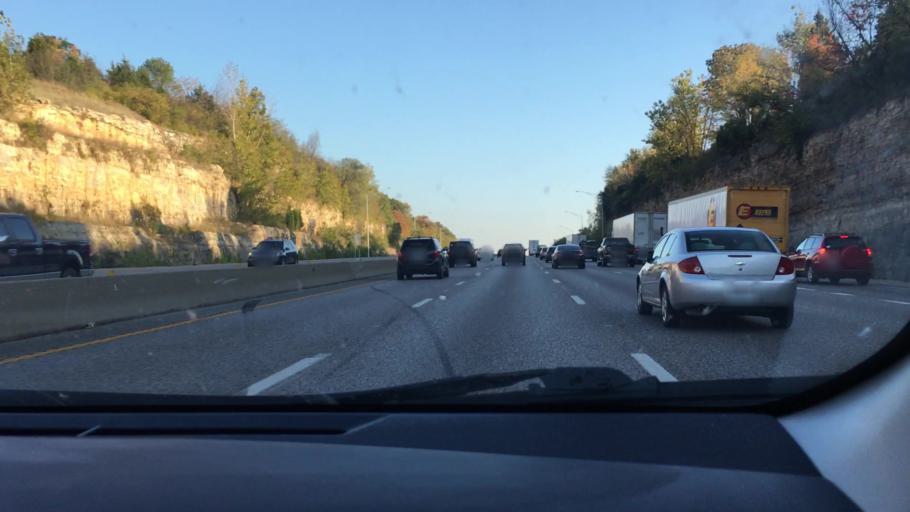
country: US
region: Missouri
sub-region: Saint Louis County
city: Sunset Hills
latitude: 38.5587
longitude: -90.4364
